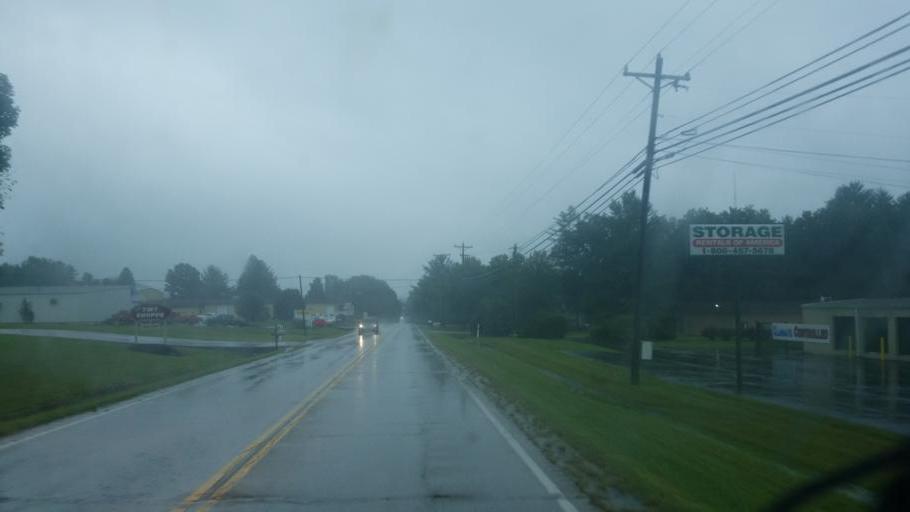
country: US
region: Kentucky
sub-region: Rowan County
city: Morehead
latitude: 38.2300
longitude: -83.4967
